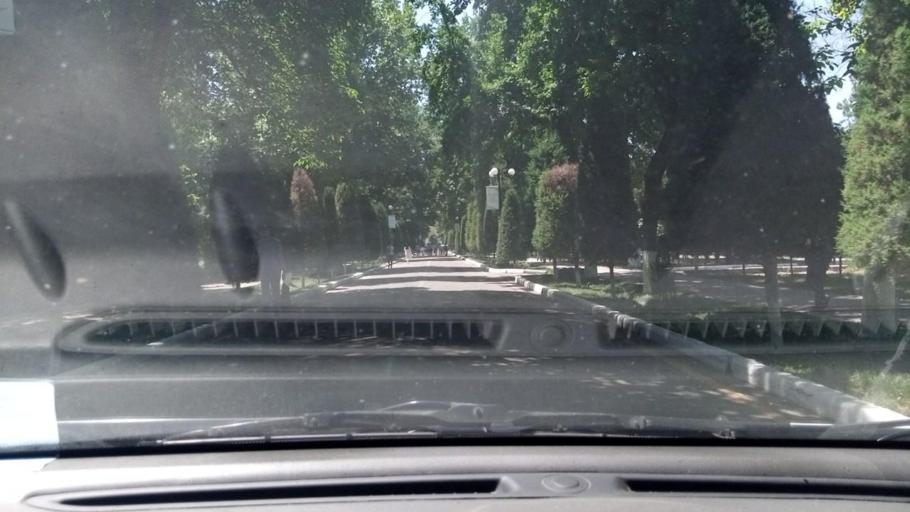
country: UZ
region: Toshkent Shahri
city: Tashkent
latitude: 41.2761
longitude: 69.2808
